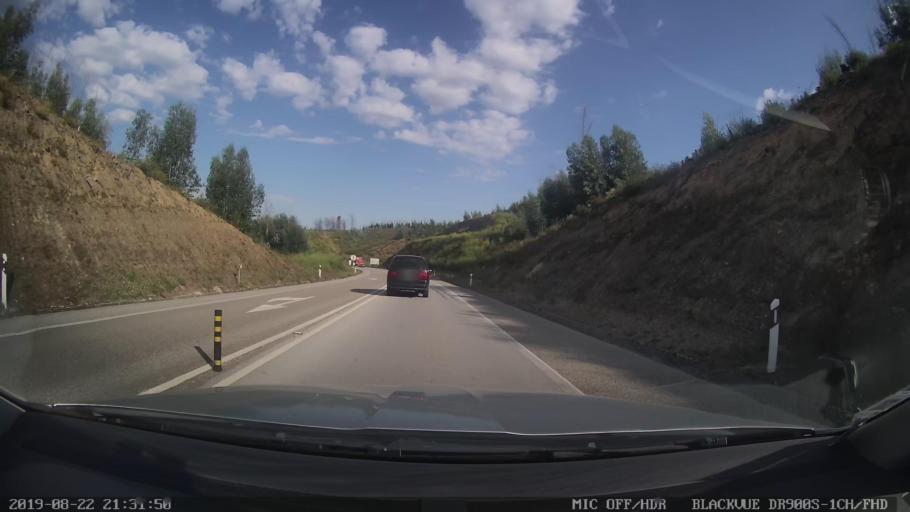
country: PT
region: Leiria
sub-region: Pedrogao Grande
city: Pedrogao Grande
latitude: 39.9240
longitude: -8.1569
